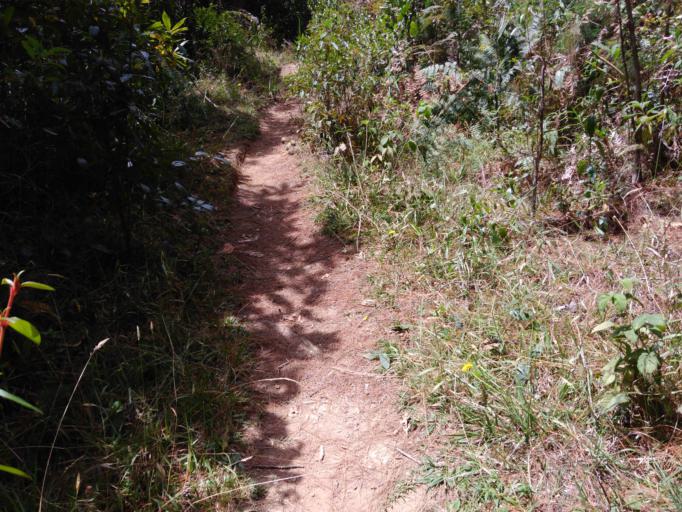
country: CO
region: Antioquia
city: Guarne
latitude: 6.2561
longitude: -75.4995
